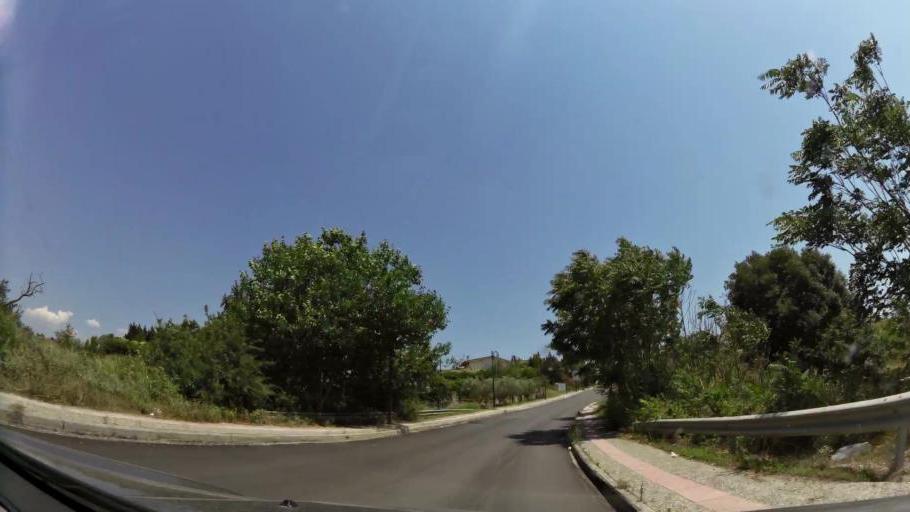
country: GR
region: Central Macedonia
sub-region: Nomos Thessalonikis
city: Plagiari
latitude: 40.4698
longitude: 22.9638
